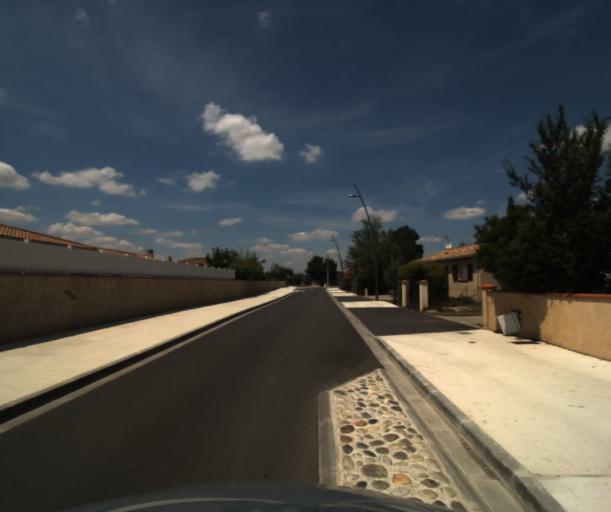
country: FR
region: Midi-Pyrenees
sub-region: Departement de la Haute-Garonne
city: Saint-Lys
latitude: 43.5050
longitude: 1.1770
